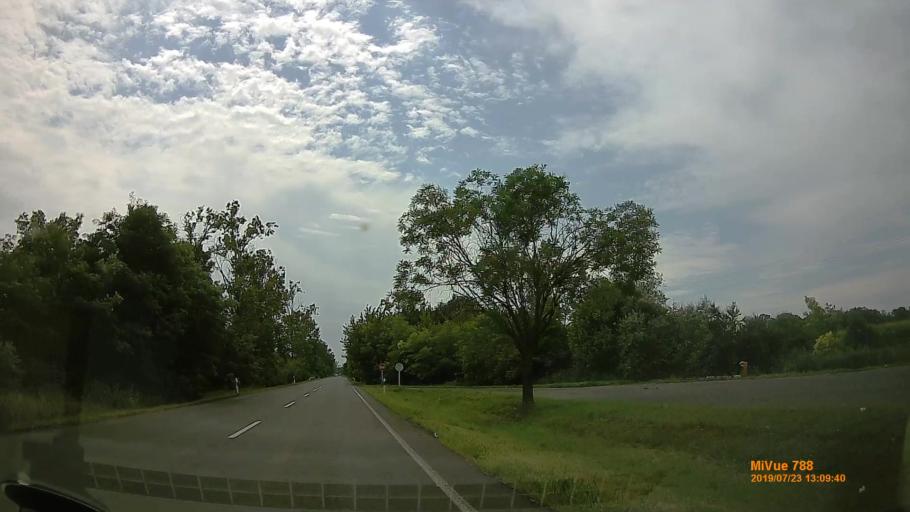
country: HU
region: Szabolcs-Szatmar-Bereg
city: Tiszavasvari
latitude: 47.9350
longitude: 21.3032
